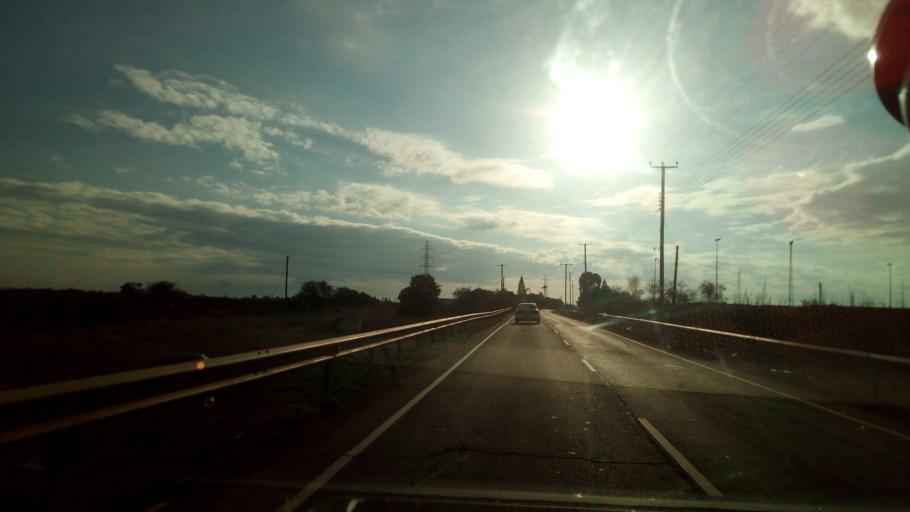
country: CY
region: Ammochostos
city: Avgorou
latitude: 35.0215
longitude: 33.8307
